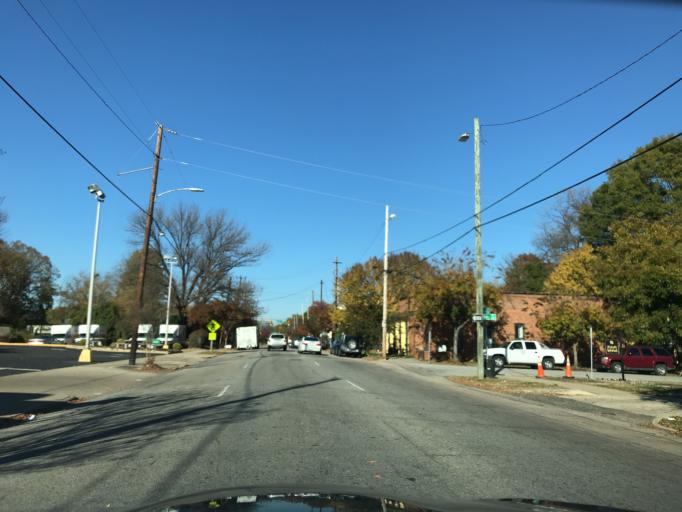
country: US
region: North Carolina
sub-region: Wake County
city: Raleigh
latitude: 35.7876
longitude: -78.6345
